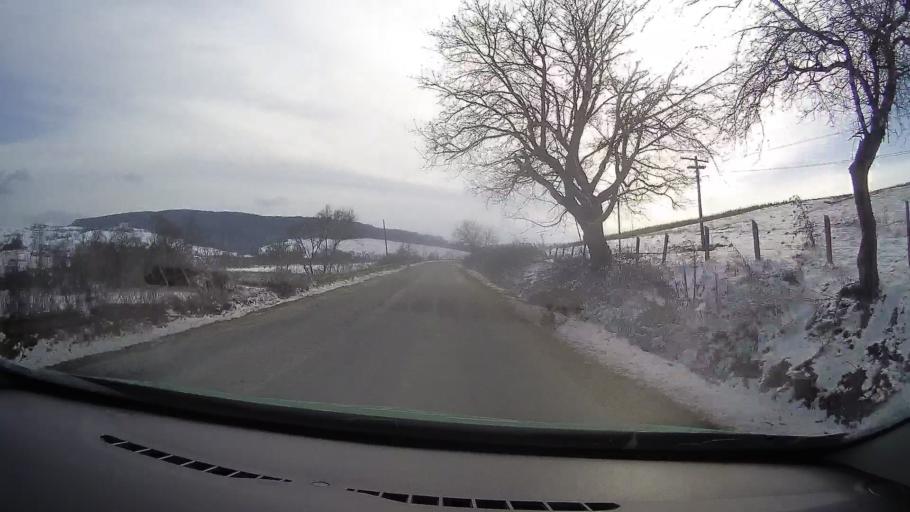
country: RO
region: Sibiu
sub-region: Oras Agnita
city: Ruja
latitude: 45.9989
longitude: 24.6728
